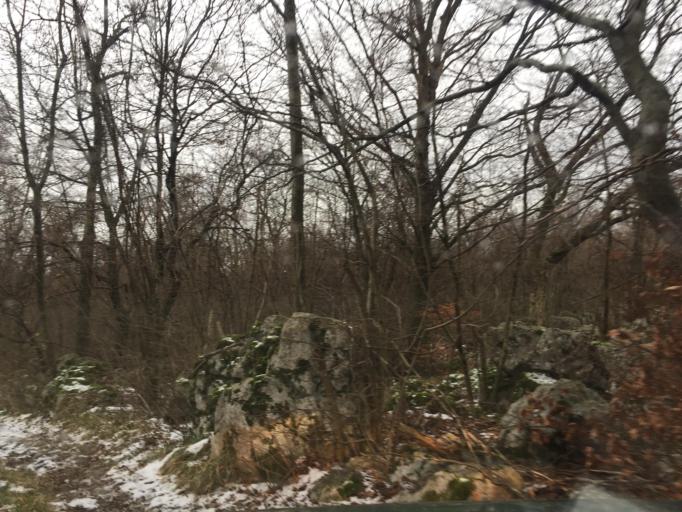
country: SI
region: Kanal
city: Kanal
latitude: 46.0581
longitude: 13.6752
